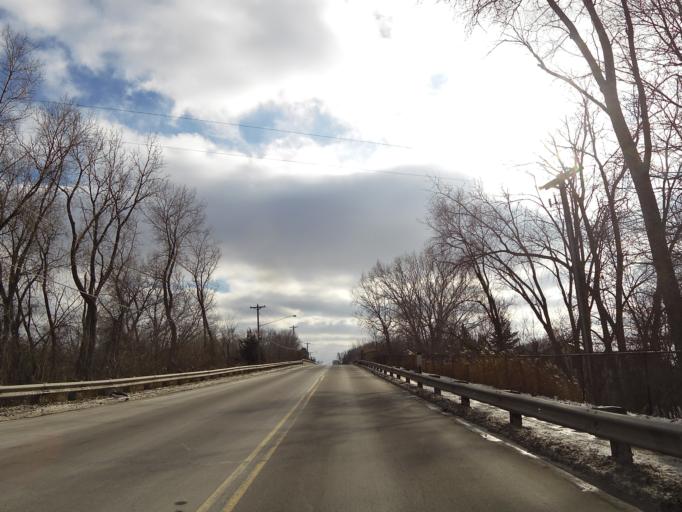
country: US
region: Minnesota
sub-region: Hennepin County
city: Eden Prairie
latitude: 44.8788
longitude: -93.4853
